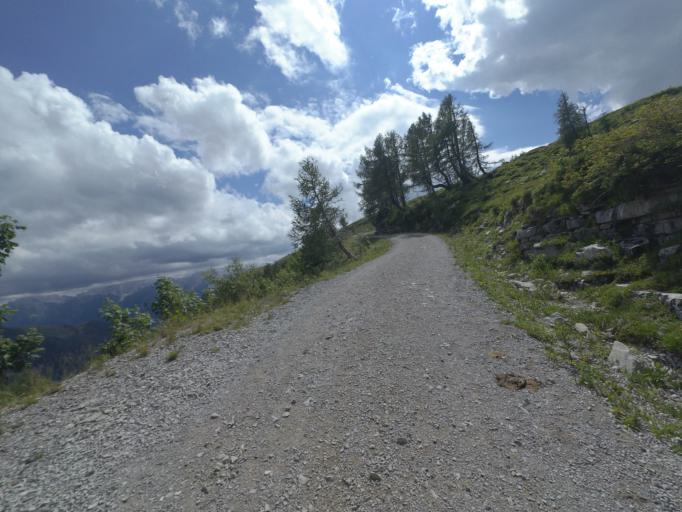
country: AT
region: Salzburg
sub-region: Politischer Bezirk Salzburg-Umgebung
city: Hintersee
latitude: 47.6564
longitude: 13.2952
